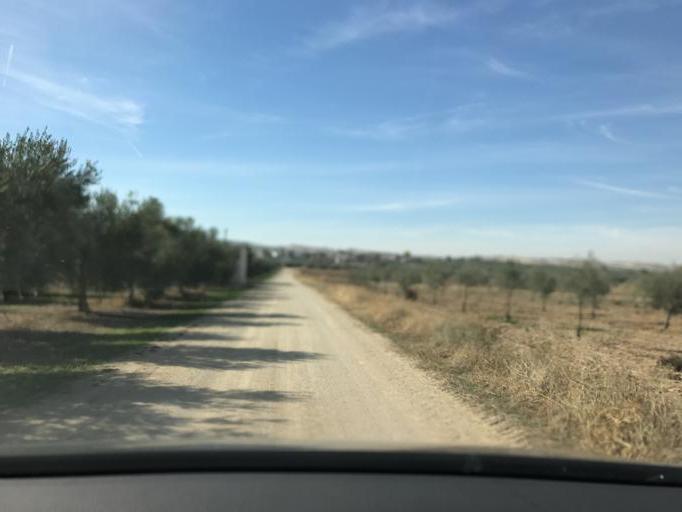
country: ES
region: Andalusia
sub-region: Provincia de Granada
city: Ventas de Huelma
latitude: 37.0866
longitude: -3.7969
